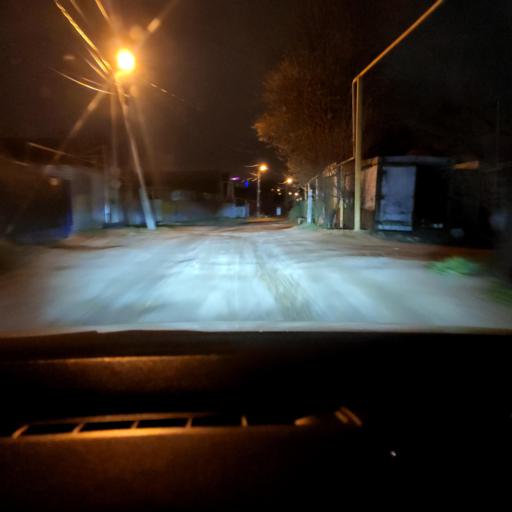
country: RU
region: Voronezj
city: Podgornoye
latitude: 51.7385
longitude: 39.1471
